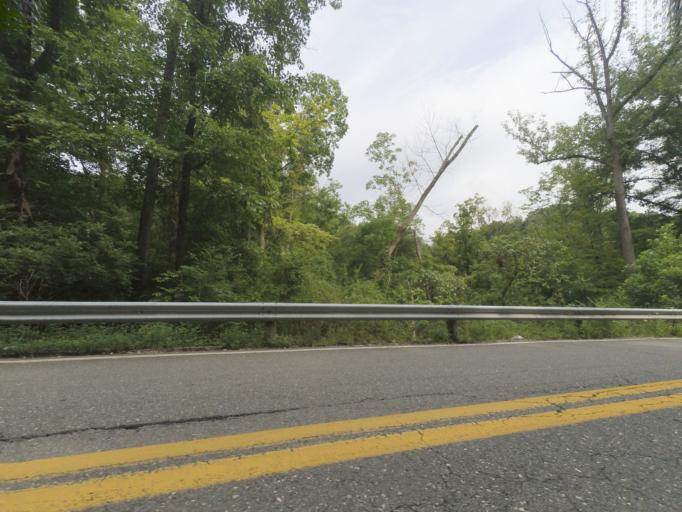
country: US
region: West Virginia
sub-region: Cabell County
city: Huntington
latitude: 38.3906
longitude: -82.4345
